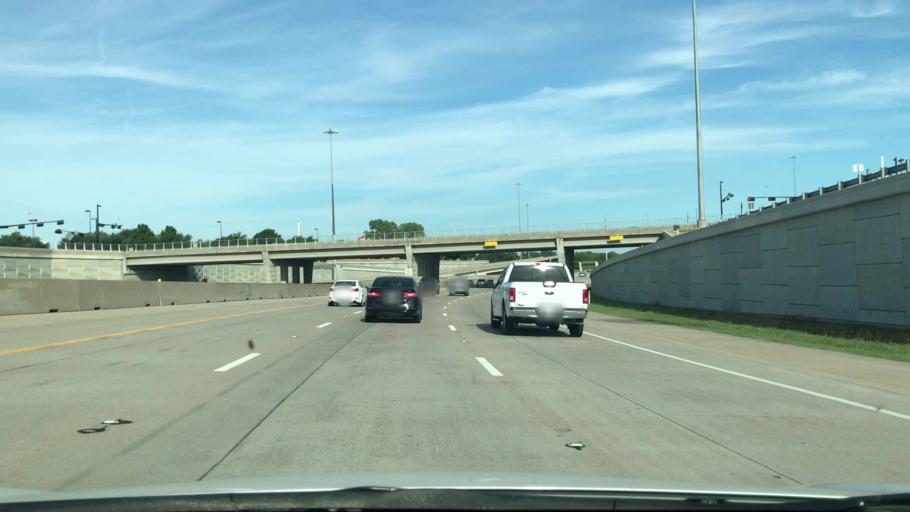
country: US
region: Texas
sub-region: Dallas County
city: Sachse
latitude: 32.9474
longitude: -96.6123
